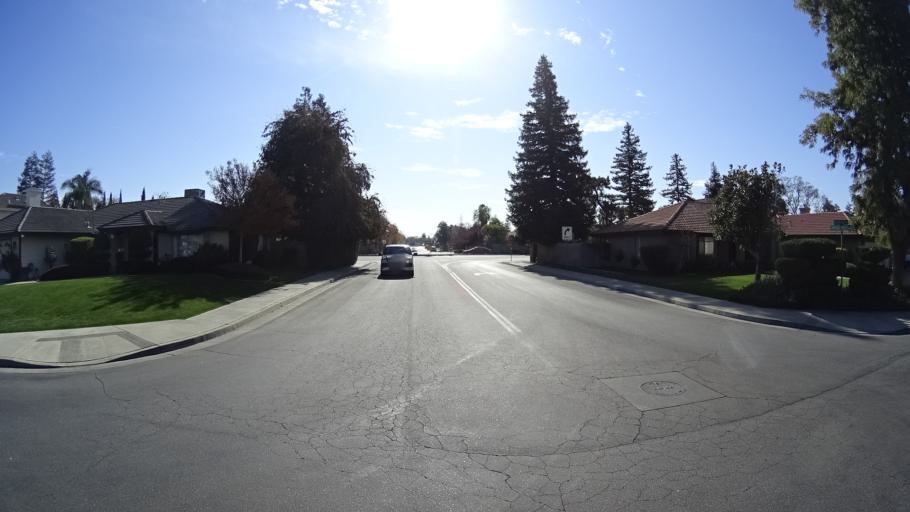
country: US
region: California
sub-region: Kern County
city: Greenacres
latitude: 35.4022
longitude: -119.0877
